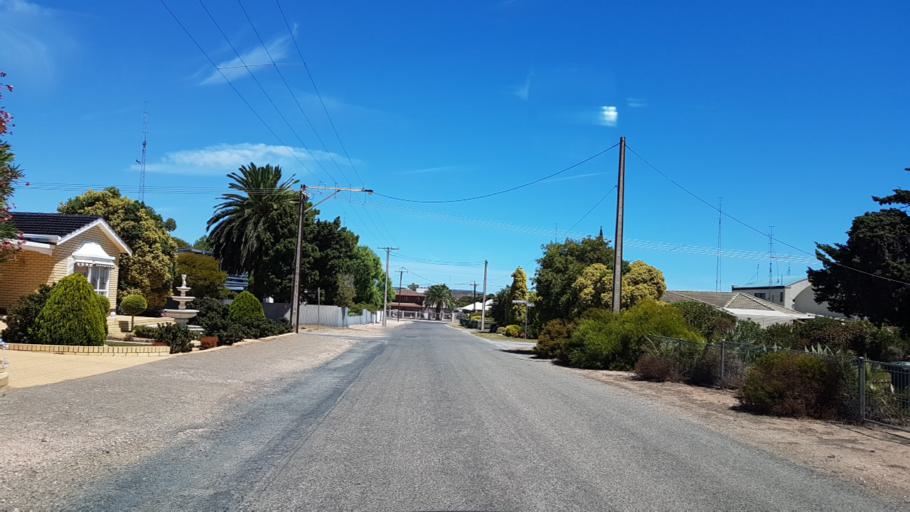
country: AU
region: South Australia
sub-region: Copper Coast
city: Wallaroo
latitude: -34.0583
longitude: 137.5610
